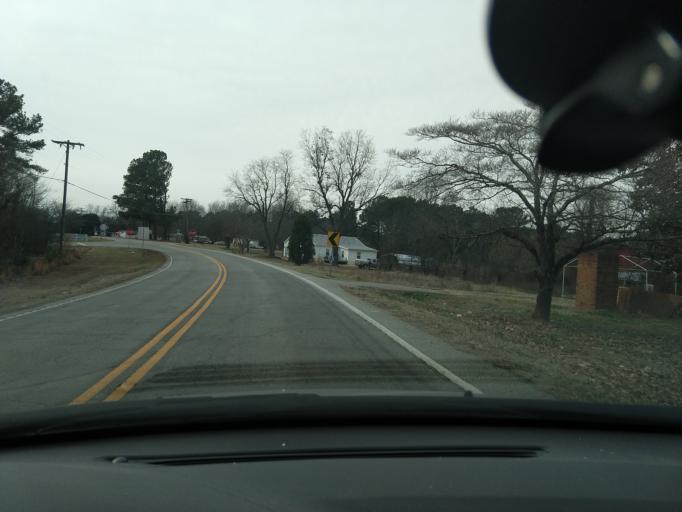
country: US
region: South Carolina
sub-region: Spartanburg County
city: Cowpens
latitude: 35.0299
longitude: -81.8214
